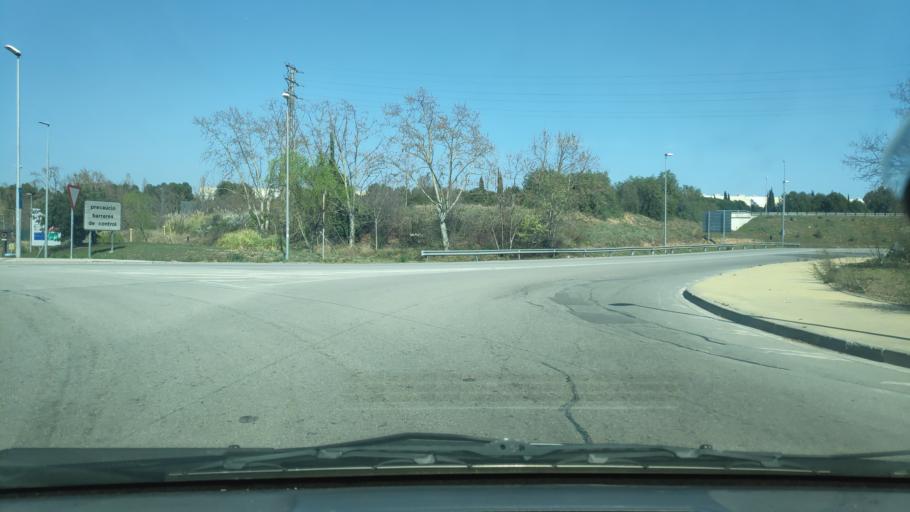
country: ES
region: Catalonia
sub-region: Provincia de Barcelona
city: Santa Perpetua de Mogoda
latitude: 41.5316
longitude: 2.1948
